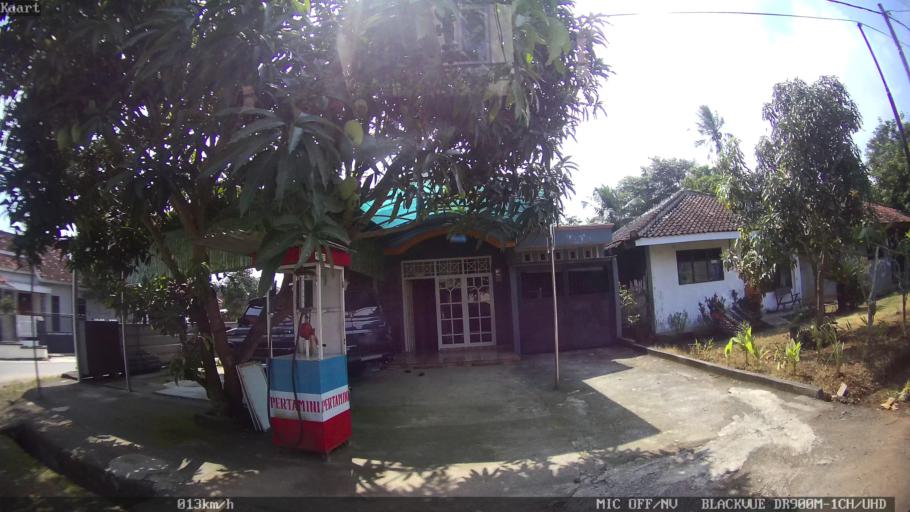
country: ID
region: Lampung
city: Kedaton
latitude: -5.3289
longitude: 105.2760
